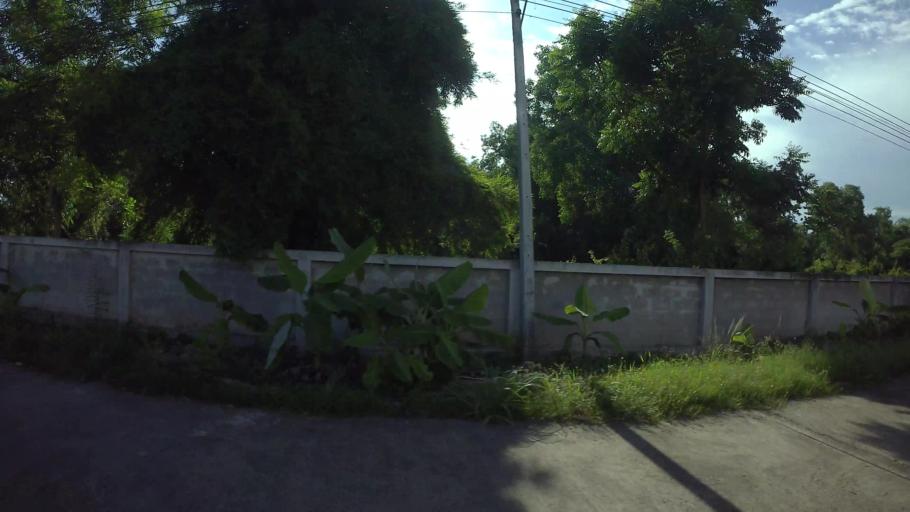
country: TH
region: Rayong
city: Rayong
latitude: 12.6716
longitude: 101.2975
